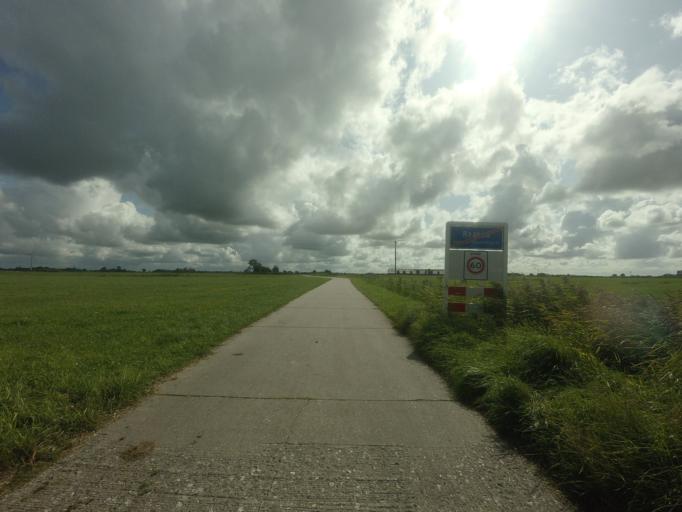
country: NL
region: Friesland
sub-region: Sudwest Fryslan
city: Scharnegoutum
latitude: 53.0750
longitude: 5.6368
